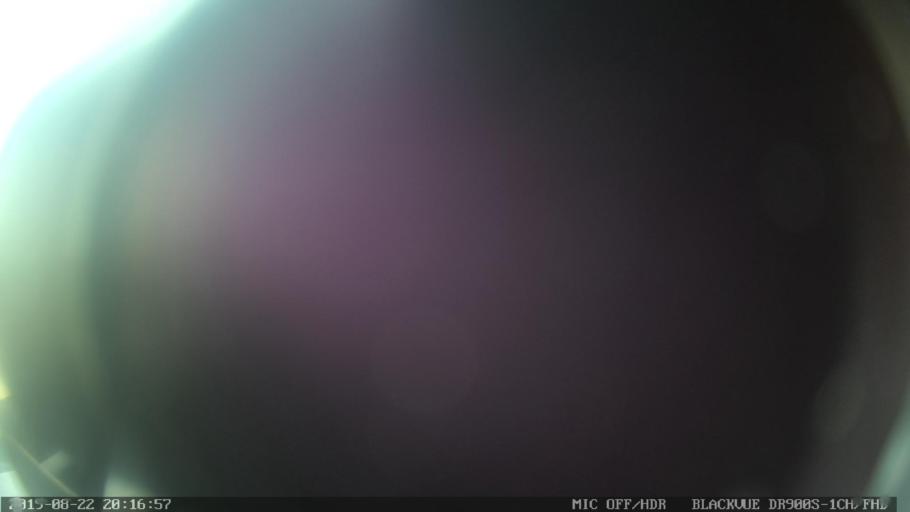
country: PT
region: Guarda
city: Alcains
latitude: 39.9241
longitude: -7.4621
